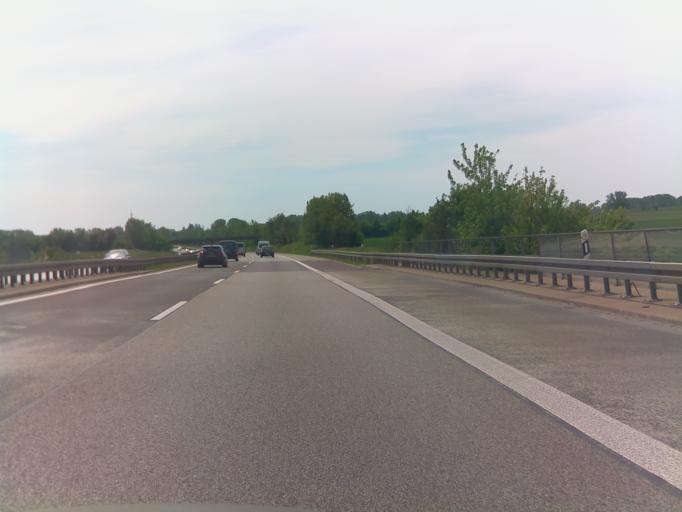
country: DE
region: Saxony-Anhalt
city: Niederndodeleben
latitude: 52.1231
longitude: 11.5301
